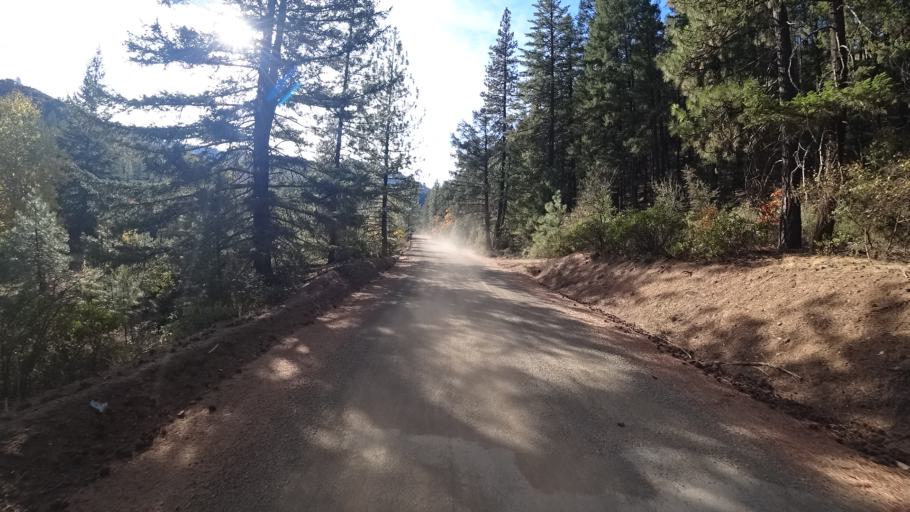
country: US
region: California
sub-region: Siskiyou County
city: Yreka
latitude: 41.6949
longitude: -122.8194
